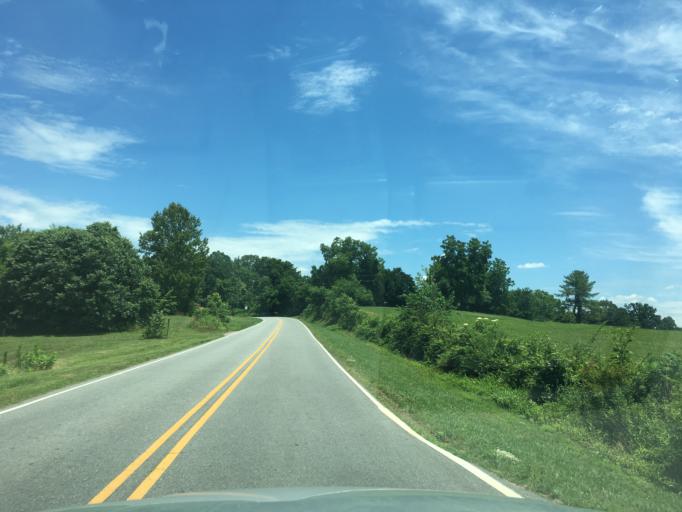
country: US
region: North Carolina
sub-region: Burke County
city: Glen Alpine
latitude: 35.6512
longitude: -81.7843
